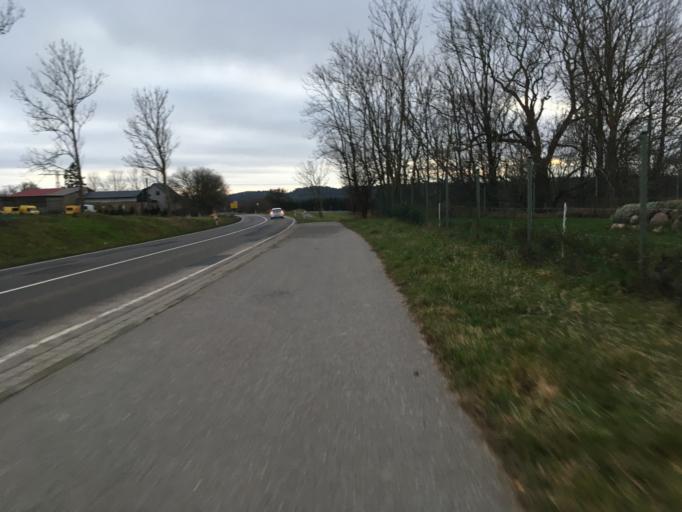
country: DE
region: Mecklenburg-Vorpommern
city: Sagard
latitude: 54.4958
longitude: 13.5789
